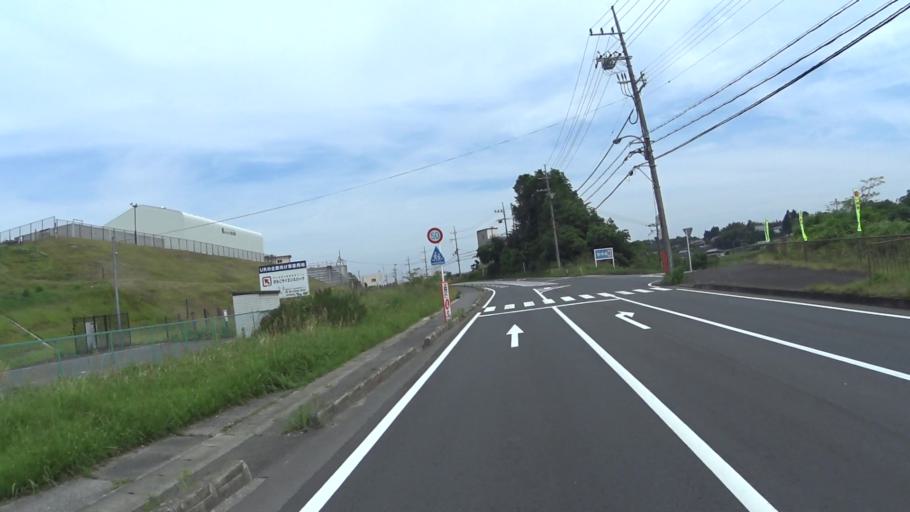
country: JP
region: Shiga Prefecture
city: Kitahama
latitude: 35.1354
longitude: 135.8844
